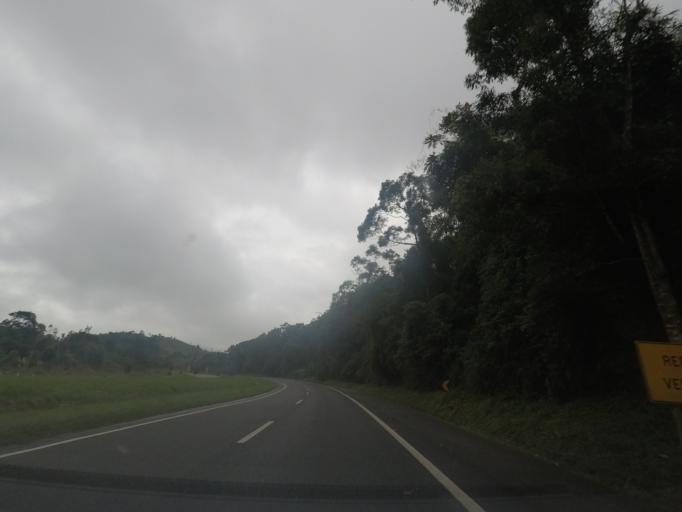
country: BR
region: Parana
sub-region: Antonina
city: Antonina
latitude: -25.0299
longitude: -48.5312
